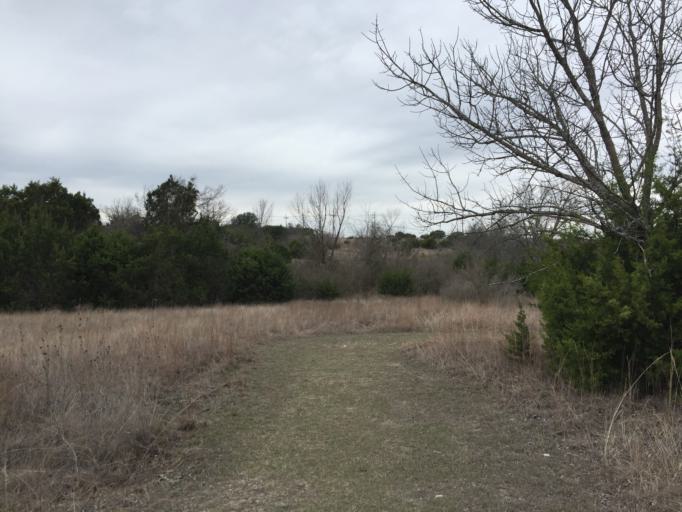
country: US
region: Texas
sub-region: Bell County
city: Fort Hood
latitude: 31.1175
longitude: -97.8140
